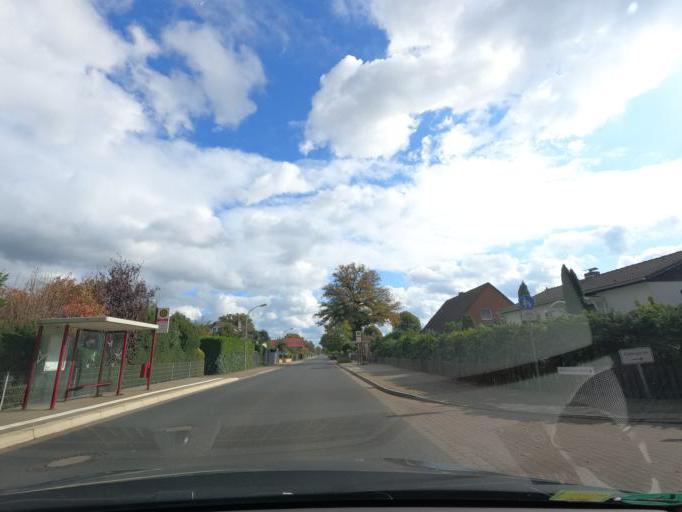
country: DE
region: Lower Saxony
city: Klein Schwulper
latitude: 52.3363
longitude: 10.4540
